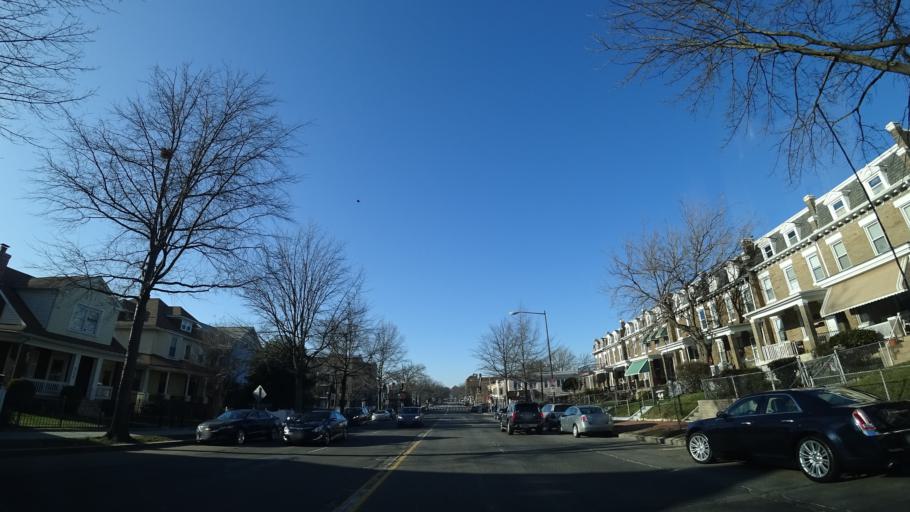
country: US
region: Maryland
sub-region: Montgomery County
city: Takoma Park
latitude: 38.9474
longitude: -77.0268
